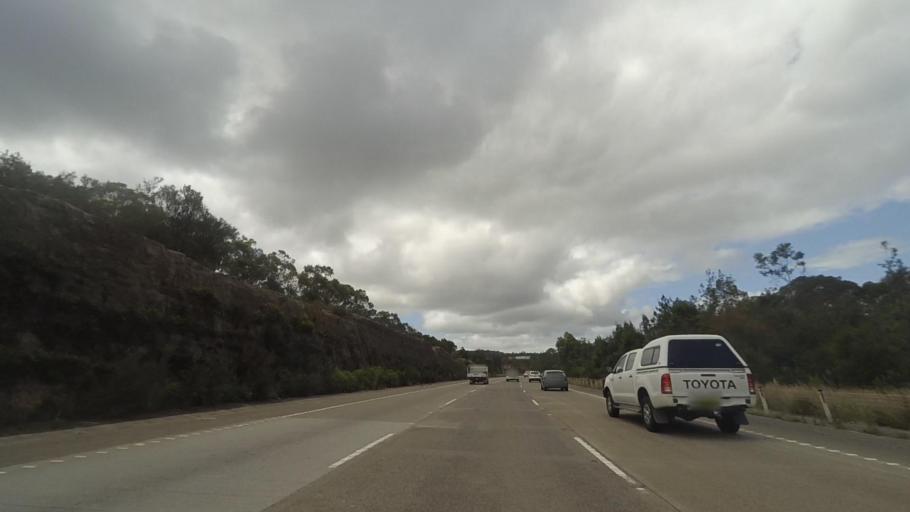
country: AU
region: New South Wales
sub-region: Gosford Shire
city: Point Clare
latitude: -33.4303
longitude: 151.2725
